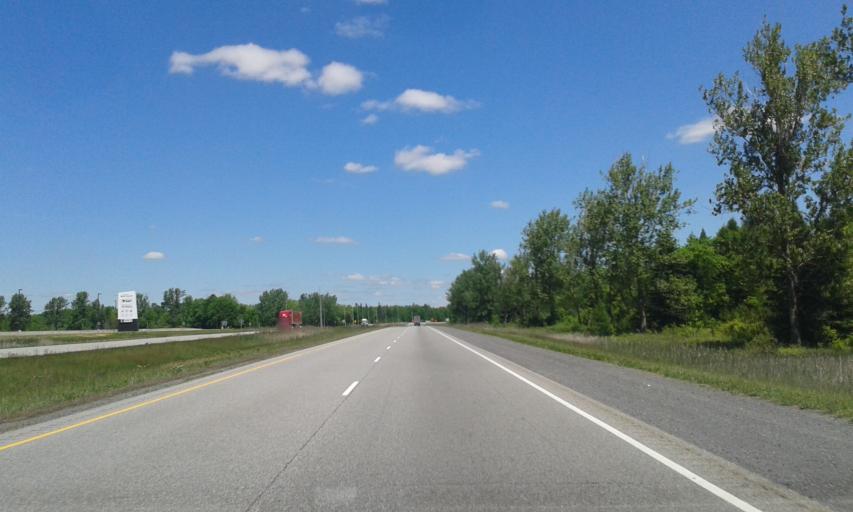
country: US
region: New York
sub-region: St. Lawrence County
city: Norfolk
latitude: 44.9692
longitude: -75.0803
